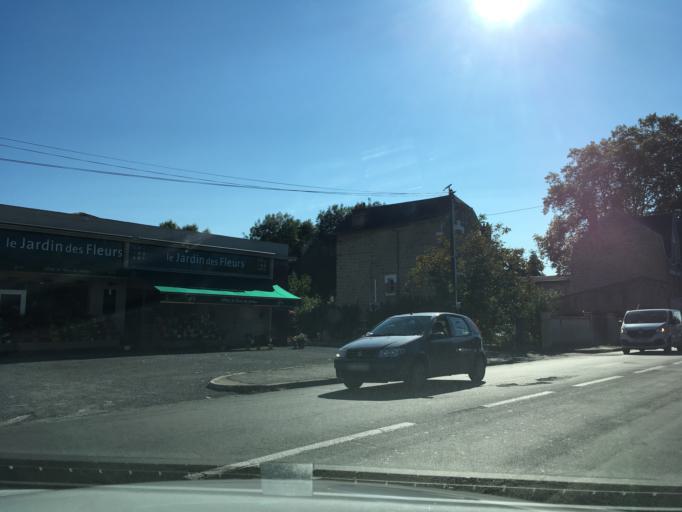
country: FR
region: Limousin
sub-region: Departement de la Correze
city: Brive-la-Gaillarde
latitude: 45.1658
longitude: 1.5387
